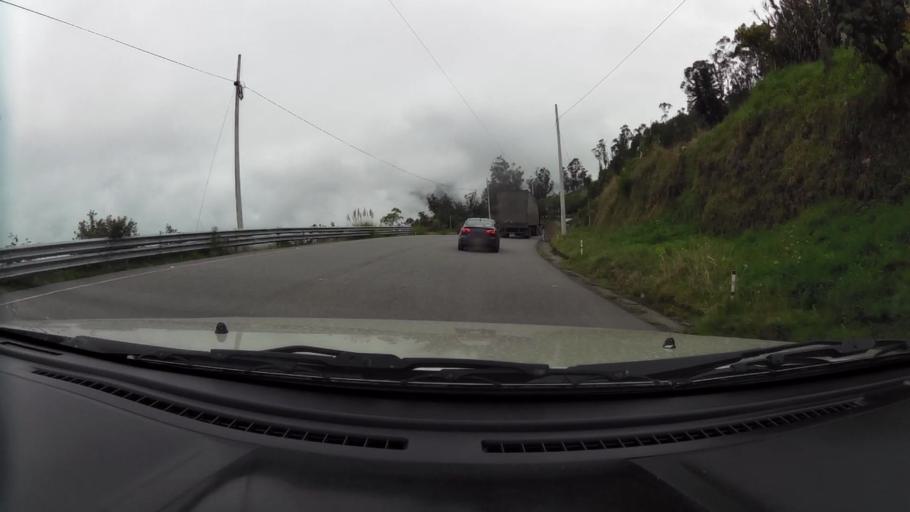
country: EC
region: Canar
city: Canar
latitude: -2.3892
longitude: -78.9731
